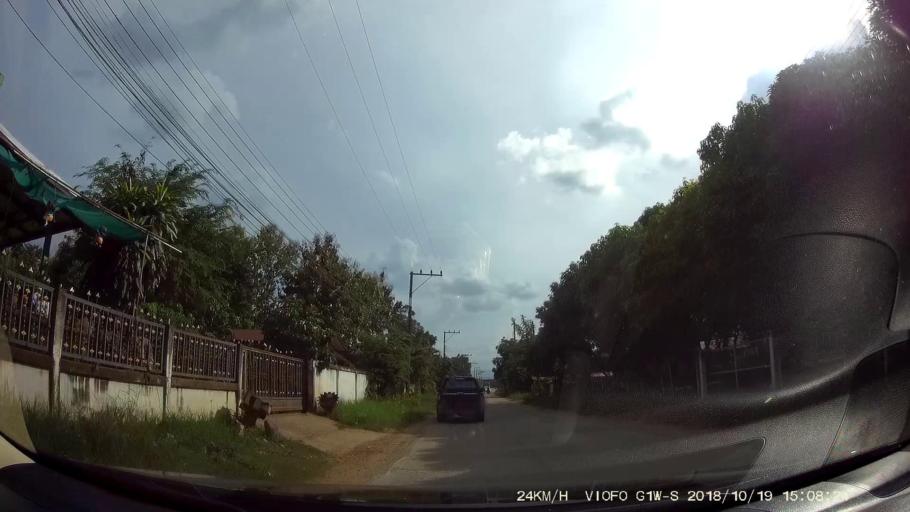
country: TH
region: Chaiyaphum
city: Phu Khiao
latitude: 16.4141
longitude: 102.1038
